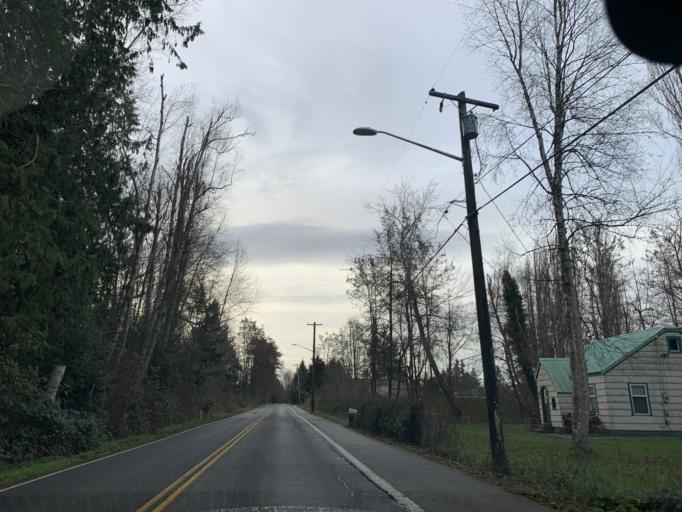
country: US
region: Washington
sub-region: Snohomish County
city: Marysville
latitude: 48.0842
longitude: -122.1565
